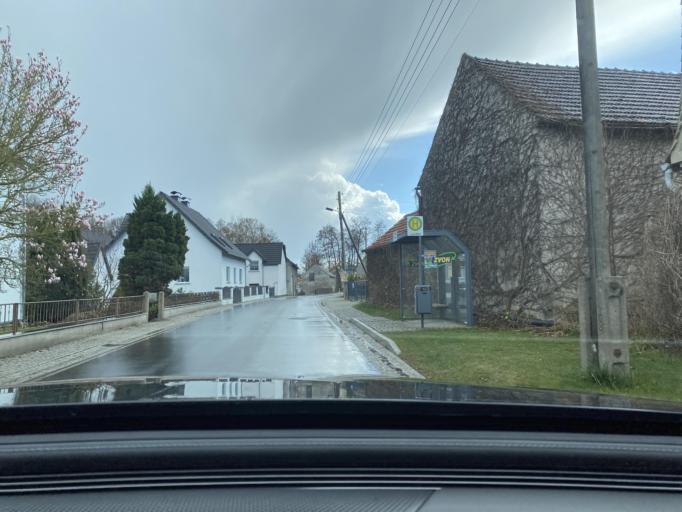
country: DE
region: Saxony
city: Grossdubrau
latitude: 51.3047
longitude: 14.4573
